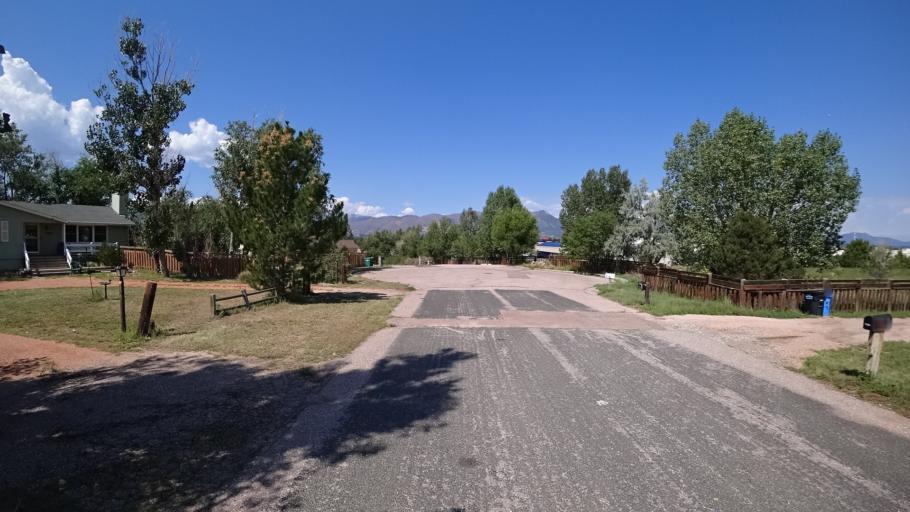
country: US
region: Colorado
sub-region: El Paso County
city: Air Force Academy
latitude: 38.9411
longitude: -104.7959
